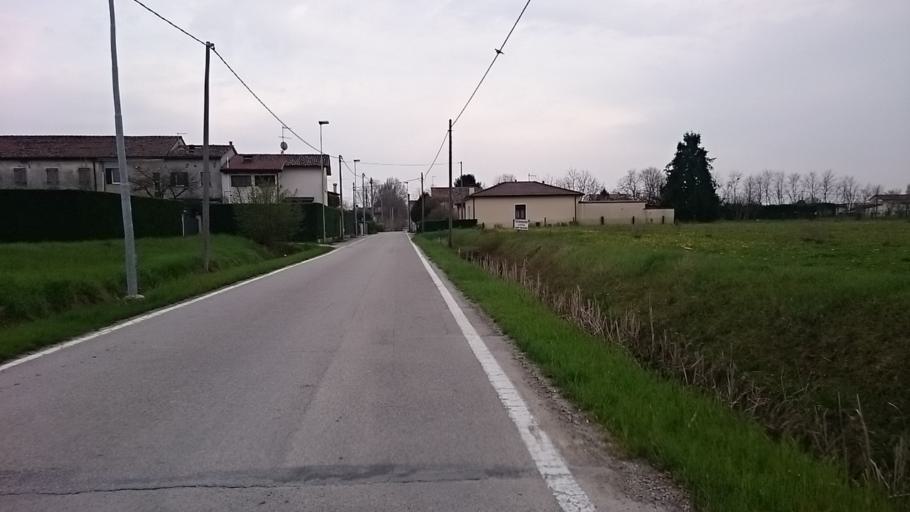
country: IT
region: Veneto
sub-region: Provincia di Padova
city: Piazzola sul Brenta
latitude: 45.5322
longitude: 11.7947
